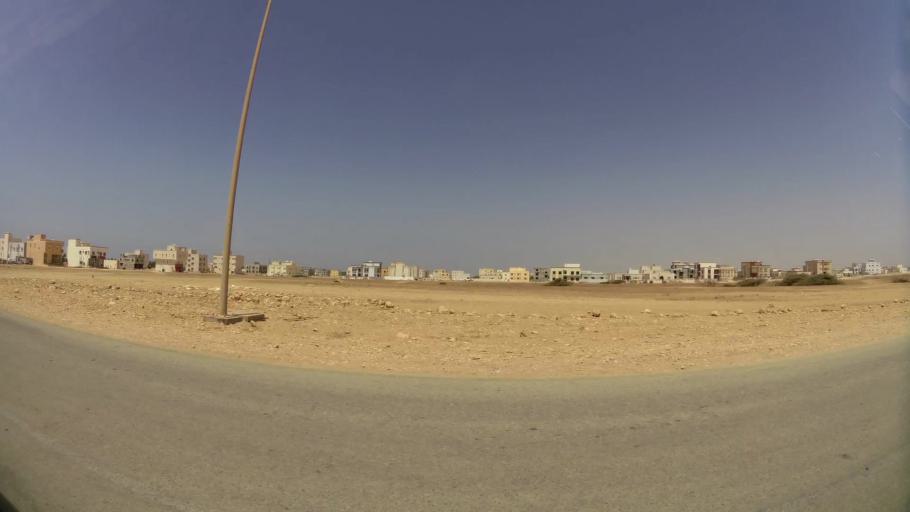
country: OM
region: Zufar
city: Salalah
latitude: 17.0525
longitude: 54.2109
